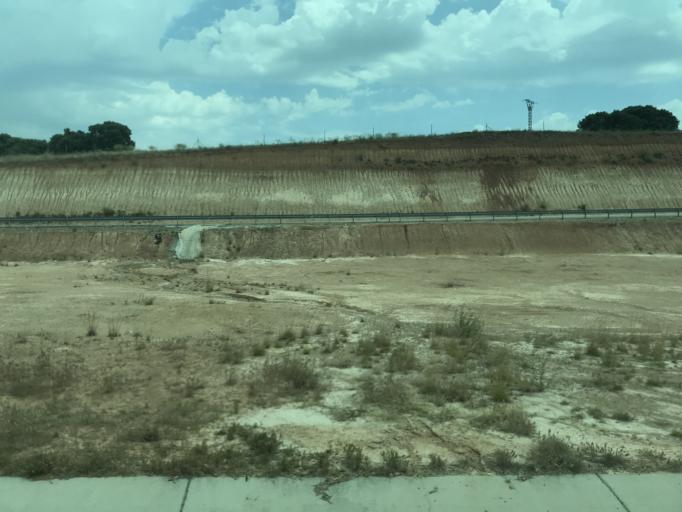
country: ES
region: Castille and Leon
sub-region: Provincia de Burgos
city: Cogollos
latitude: 42.2075
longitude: -3.7006
